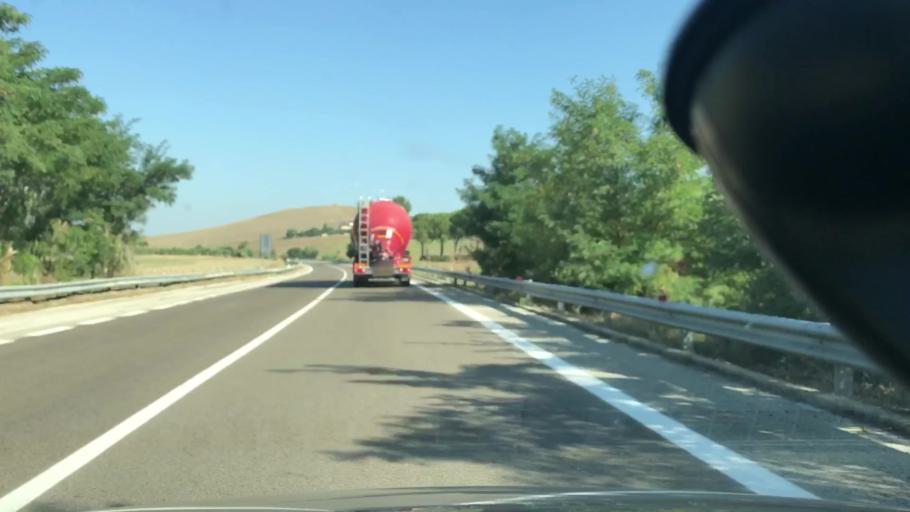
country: IT
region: Basilicate
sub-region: Provincia di Matera
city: Irsina
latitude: 40.8052
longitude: 16.2734
